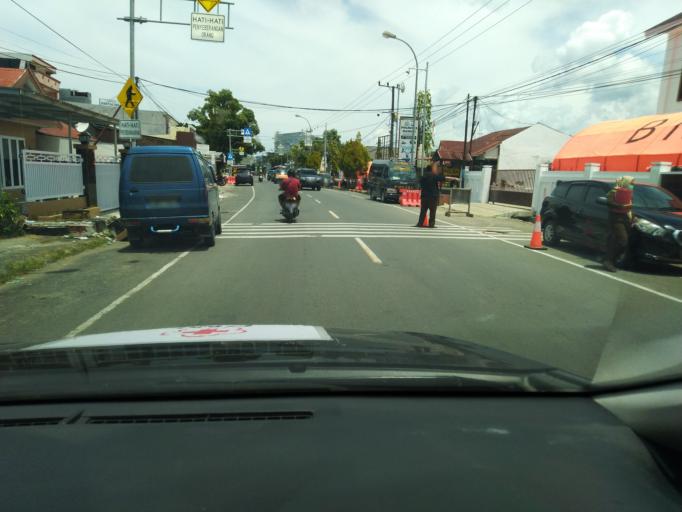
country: ID
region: Sulawesi Barat
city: Mamuju
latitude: -2.6777
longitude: 118.8830
